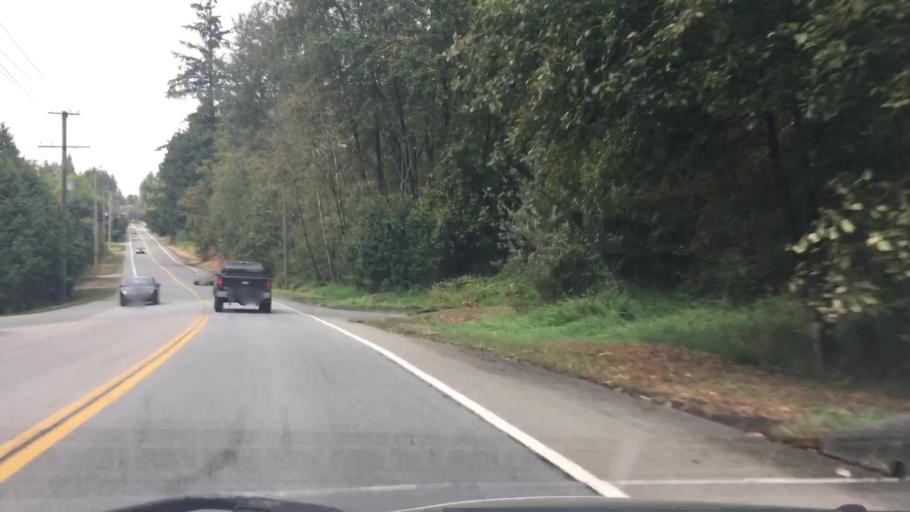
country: CA
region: British Columbia
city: Langley
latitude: 49.1040
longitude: -122.5719
